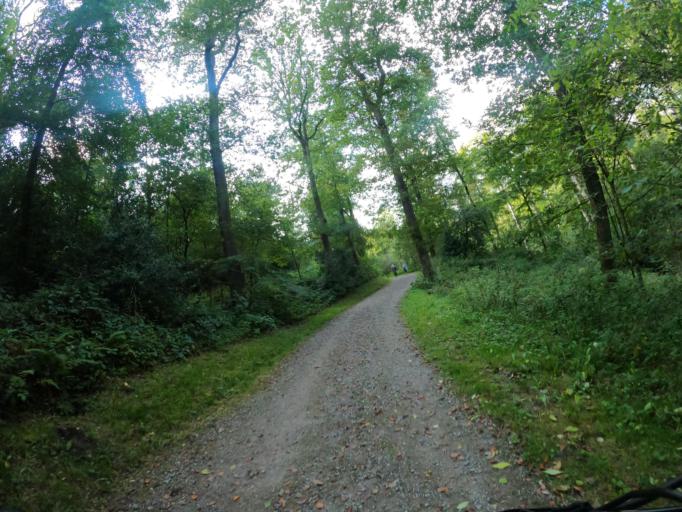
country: DE
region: North Rhine-Westphalia
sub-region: Regierungsbezirk Dusseldorf
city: Essen
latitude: 51.4131
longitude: 7.0422
